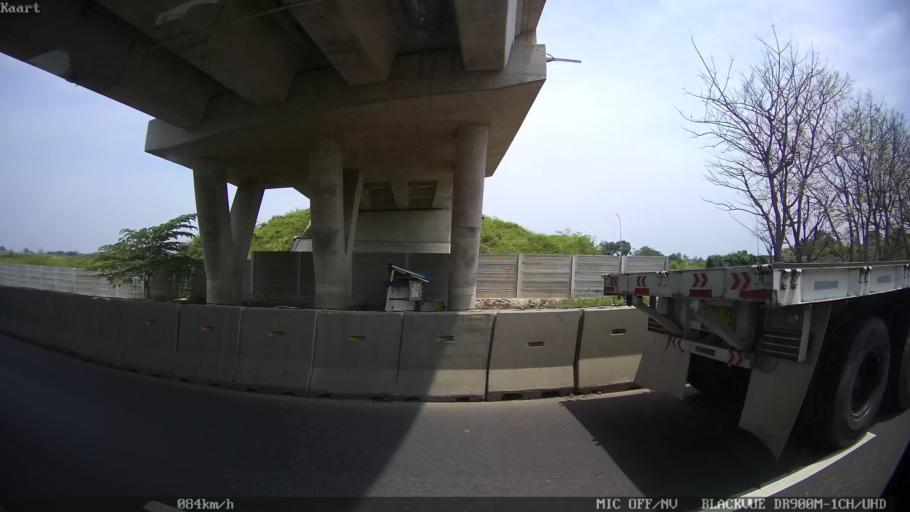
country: ID
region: Banten
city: Serang
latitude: -6.1388
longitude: 106.2446
